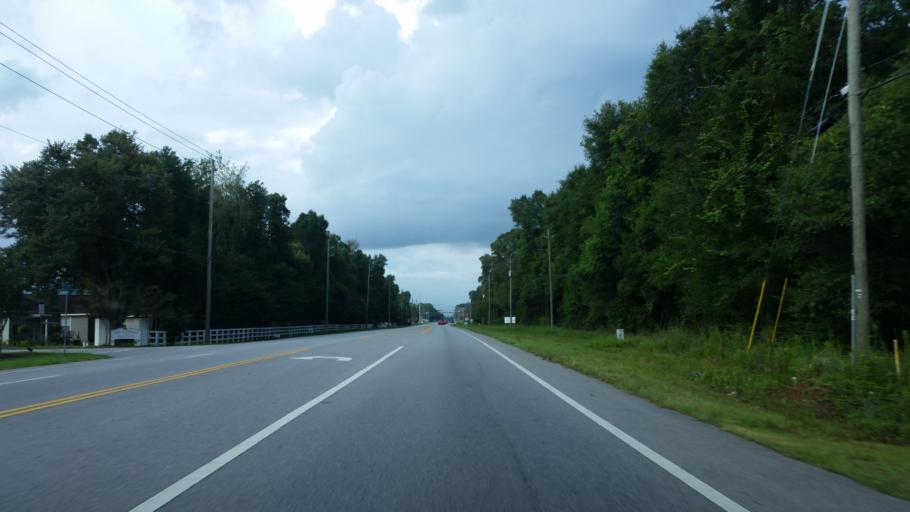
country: US
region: Florida
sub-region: Escambia County
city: Ensley
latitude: 30.5398
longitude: -87.3130
